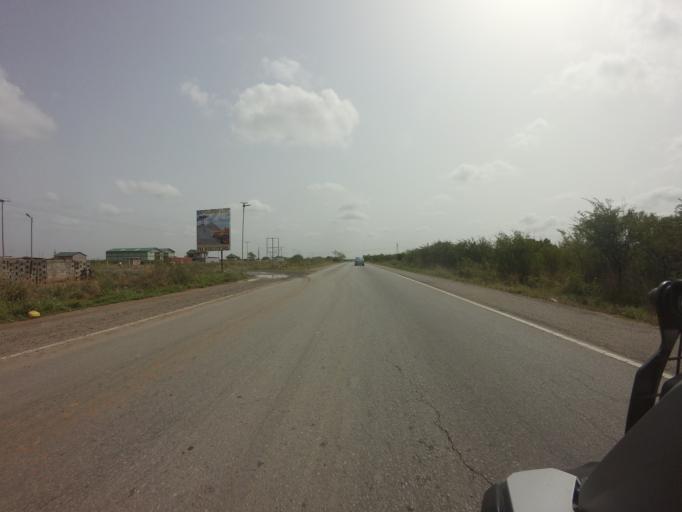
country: GH
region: Greater Accra
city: Tema
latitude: 5.7921
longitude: 0.1191
